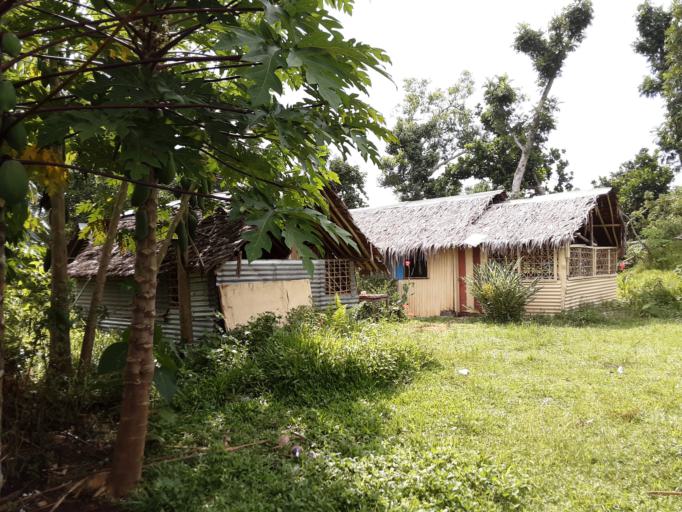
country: VU
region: Sanma
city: Luganville
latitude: -15.5802
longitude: 167.0018
